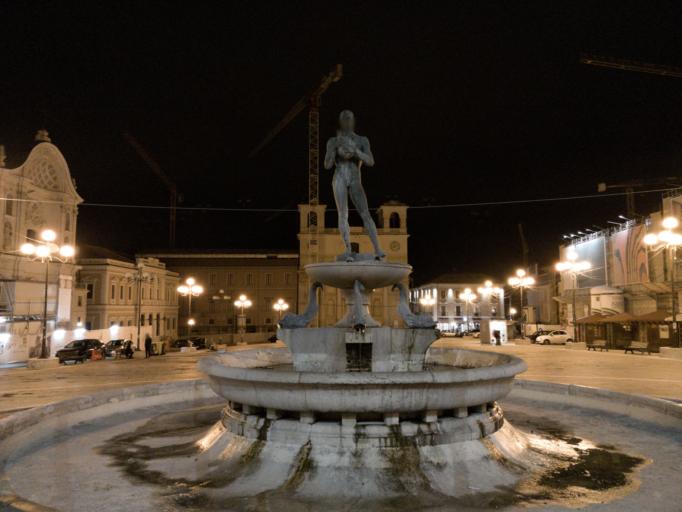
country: IT
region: Abruzzo
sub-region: Provincia dell' Aquila
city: L'Aquila
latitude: 42.3487
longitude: 13.3988
